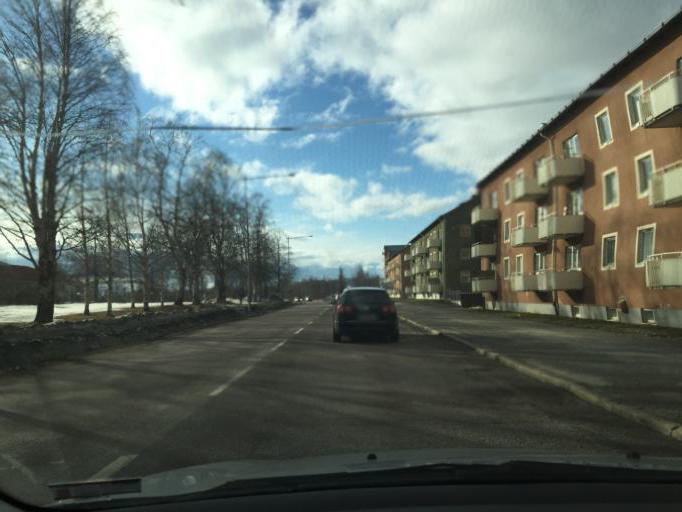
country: SE
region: Norrbotten
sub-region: Lulea Kommun
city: Lulea
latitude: 65.5797
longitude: 22.1795
